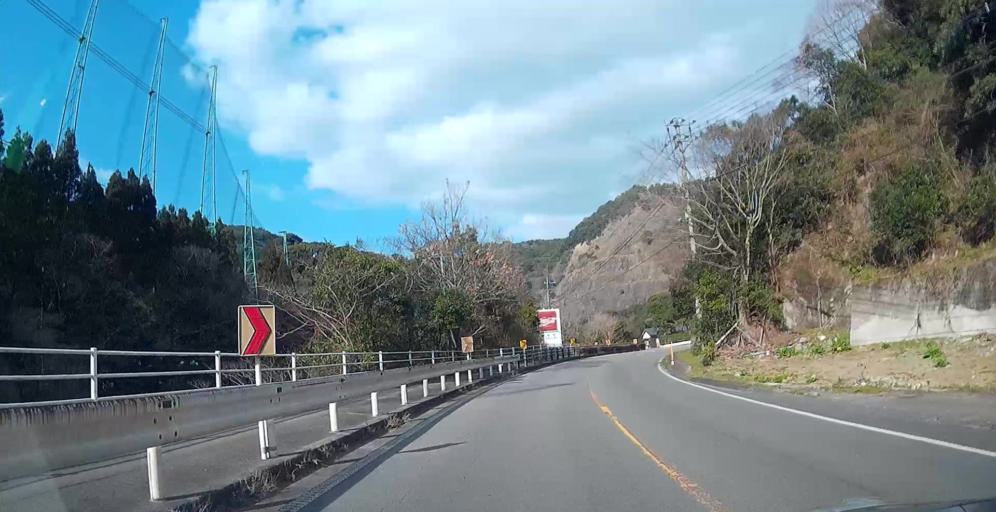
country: JP
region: Kumamoto
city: Yatsushiro
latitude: 32.4096
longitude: 130.5539
